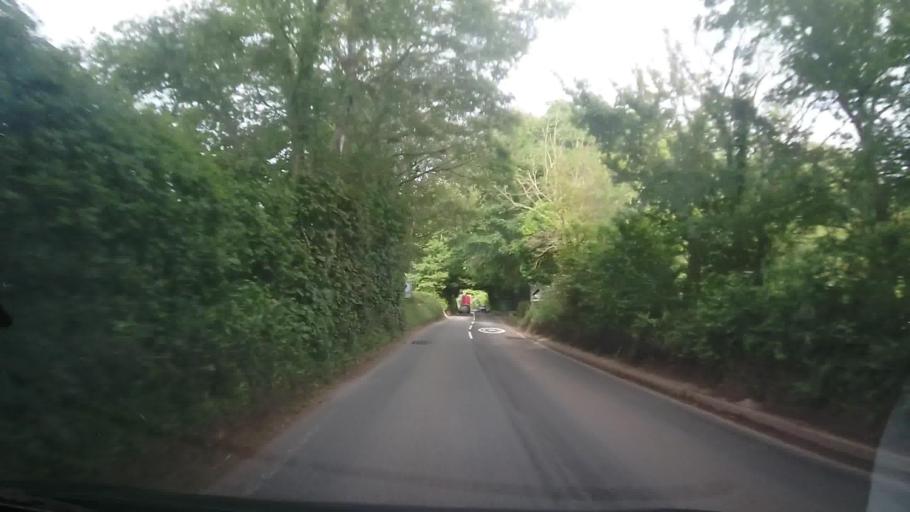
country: GB
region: England
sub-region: Devon
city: Kingsbridge
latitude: 50.2984
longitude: -3.8069
